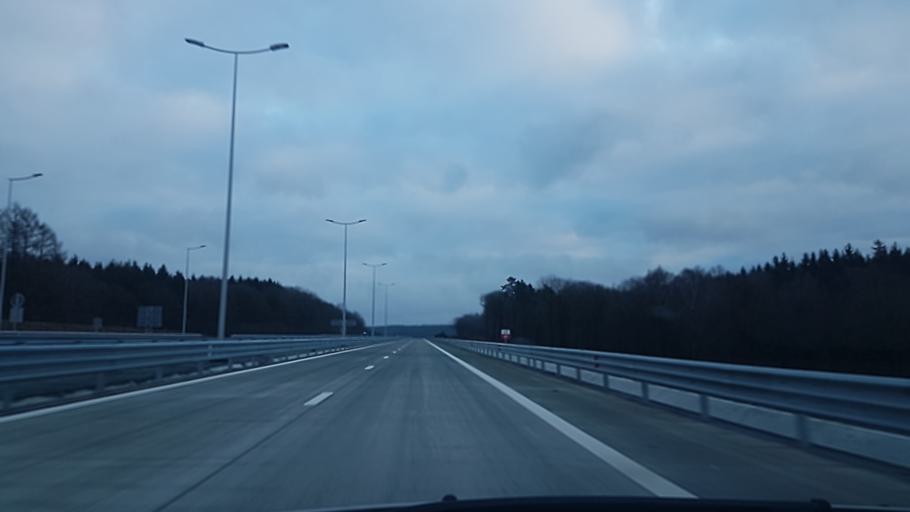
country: BE
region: Wallonia
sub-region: Province de Namur
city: Couvin
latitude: 50.0209
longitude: 4.5254
